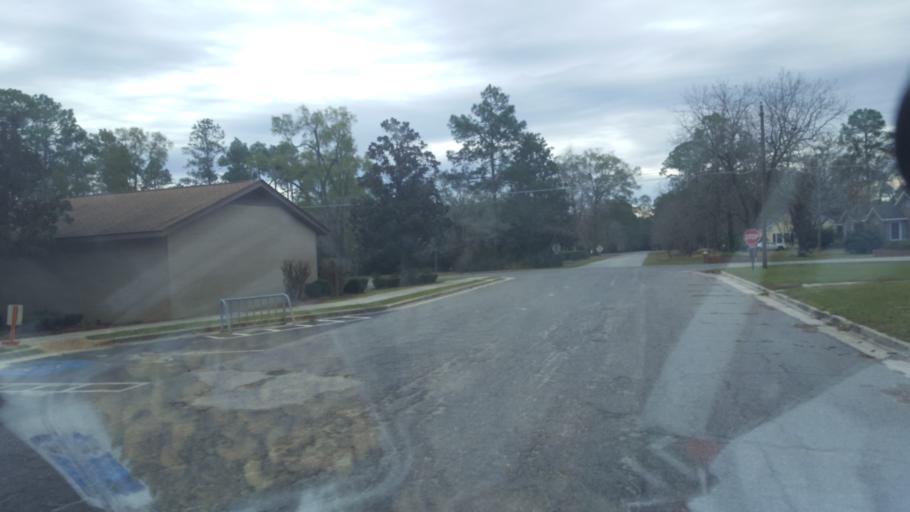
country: US
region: Georgia
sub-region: Irwin County
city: Ocilla
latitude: 31.5917
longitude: -83.2519
